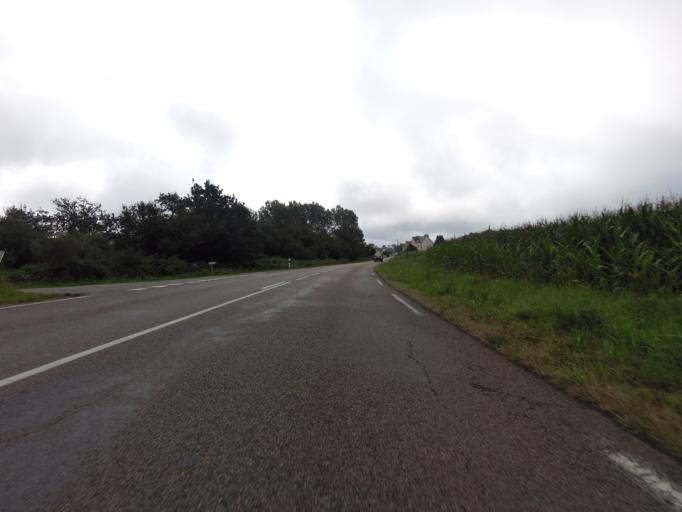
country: FR
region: Brittany
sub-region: Departement du Finistere
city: Plouhinec
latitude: 48.0078
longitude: -4.4574
